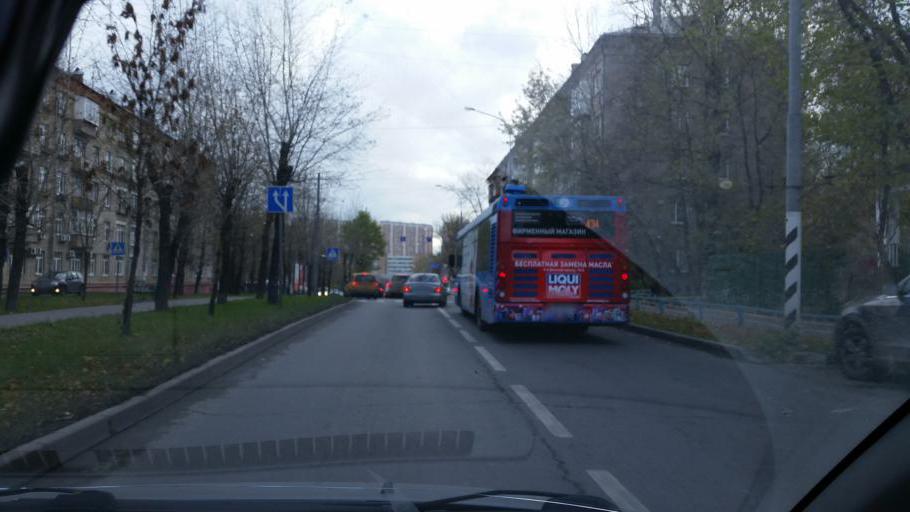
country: RU
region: Moscow
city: Kotlovka
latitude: 55.6778
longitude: 37.5980
